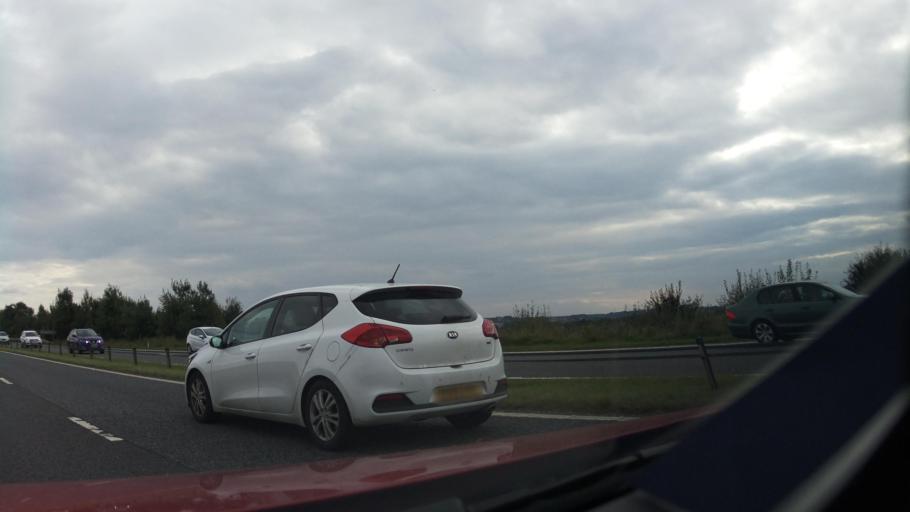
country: GB
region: England
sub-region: County Durham
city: West Cornforth
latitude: 54.7199
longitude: -1.5212
